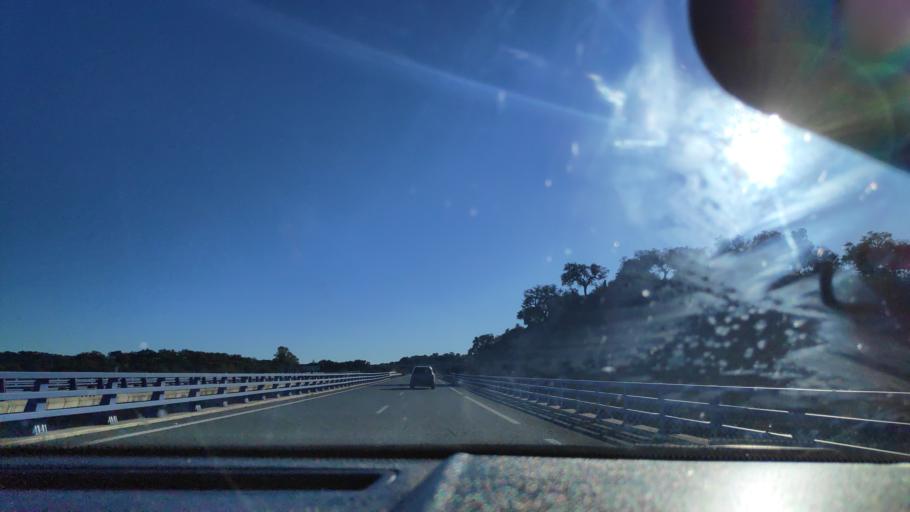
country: ES
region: Andalusia
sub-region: Provincia de Huelva
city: Santa Olalla del Cala
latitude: 37.8852
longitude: -6.2191
